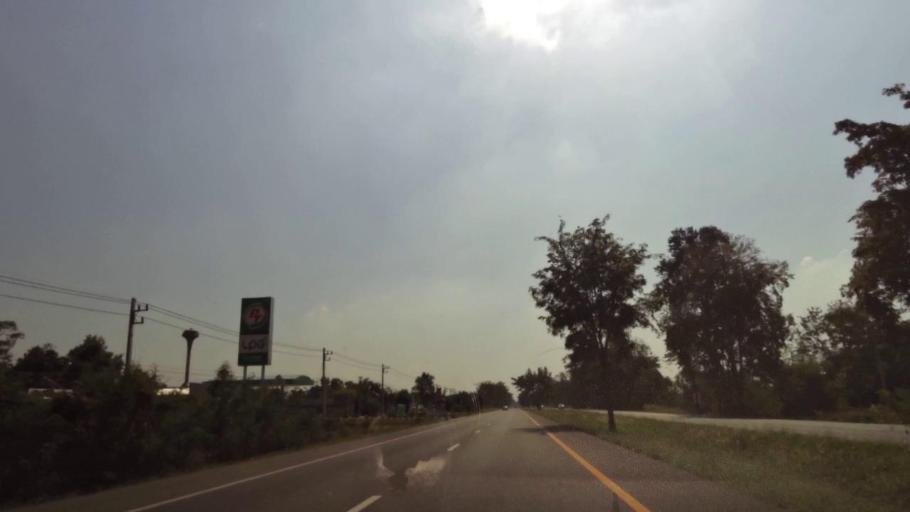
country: TH
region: Phichit
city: Bueng Na Rang
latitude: 16.2057
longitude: 100.1276
